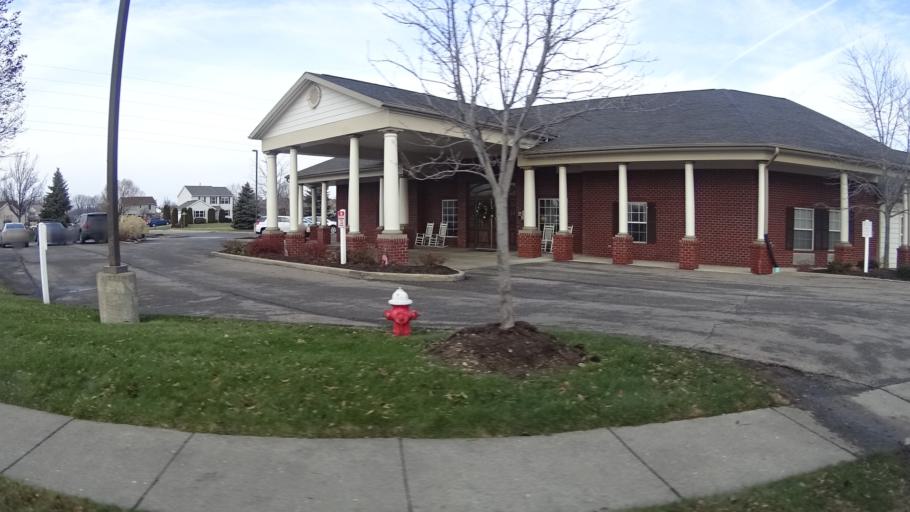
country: US
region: Ohio
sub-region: Lorain County
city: Amherst
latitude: 41.4184
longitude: -82.2164
